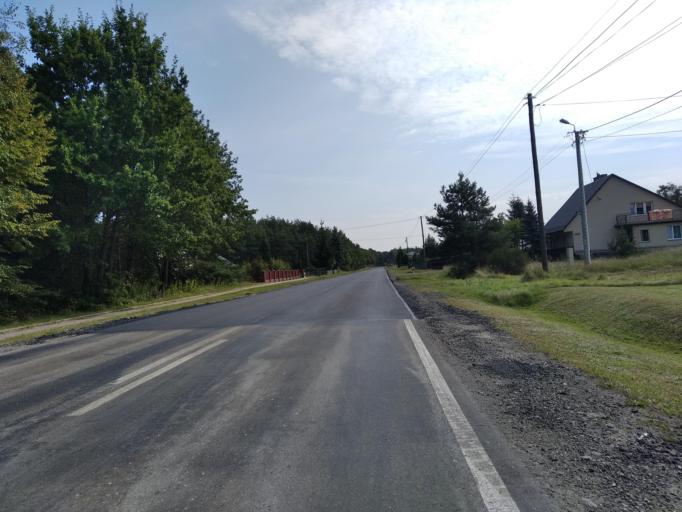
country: PL
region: Subcarpathian Voivodeship
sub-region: Powiat ropczycko-sedziszowski
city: Ostrow
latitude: 50.1580
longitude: 21.5472
